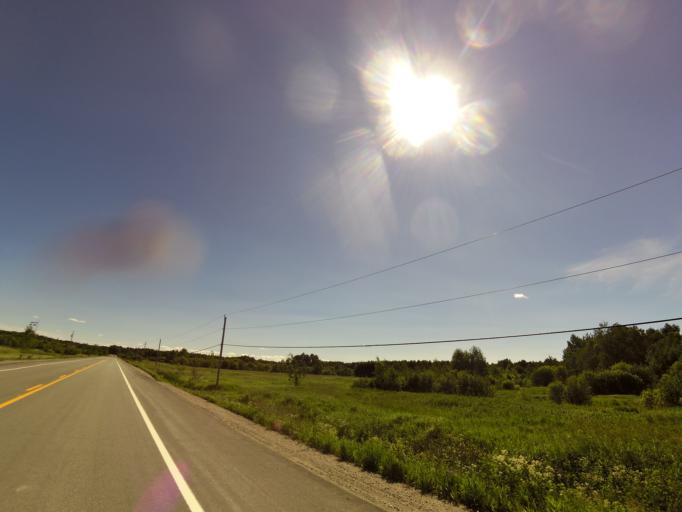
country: CA
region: Quebec
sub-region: Abitibi-Temiscamingue
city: Senneterre
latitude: 48.2059
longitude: -77.3583
